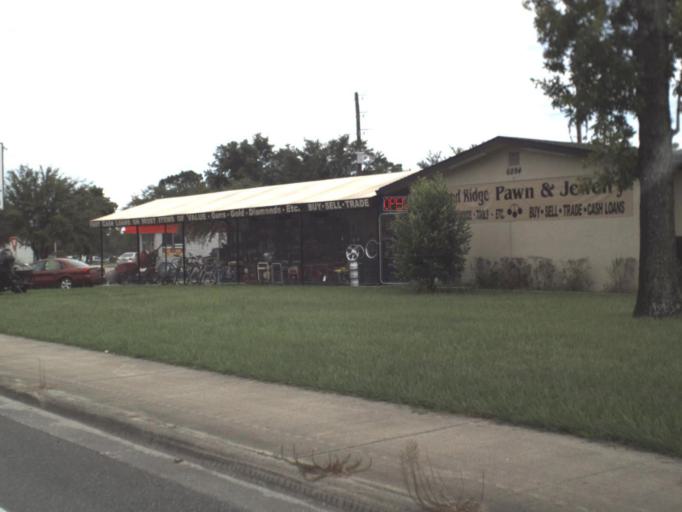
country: US
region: Florida
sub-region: Citrus County
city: Crystal River
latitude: 28.8920
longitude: -82.5496
